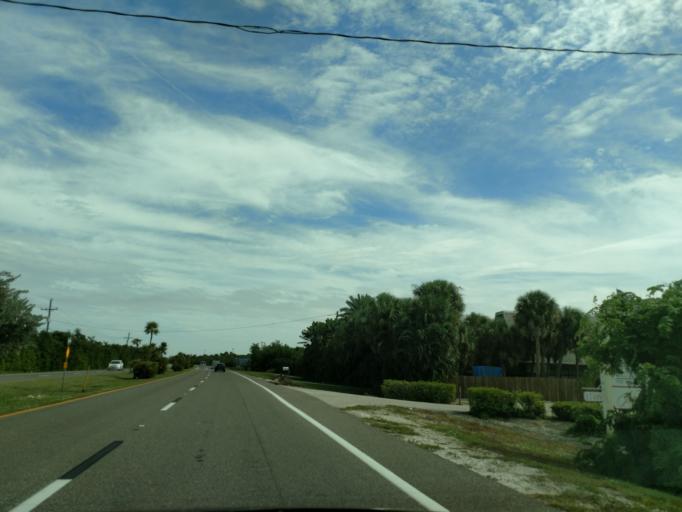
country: US
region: Florida
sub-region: Lee County
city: Punta Rassa
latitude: 26.4853
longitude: -81.9989
